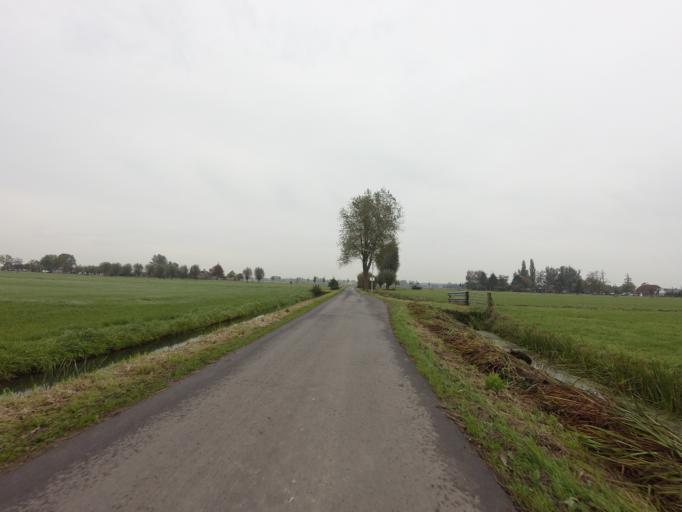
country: NL
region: Utrecht
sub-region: Gemeente Vianen
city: Vianen
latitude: 51.9494
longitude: 5.1418
